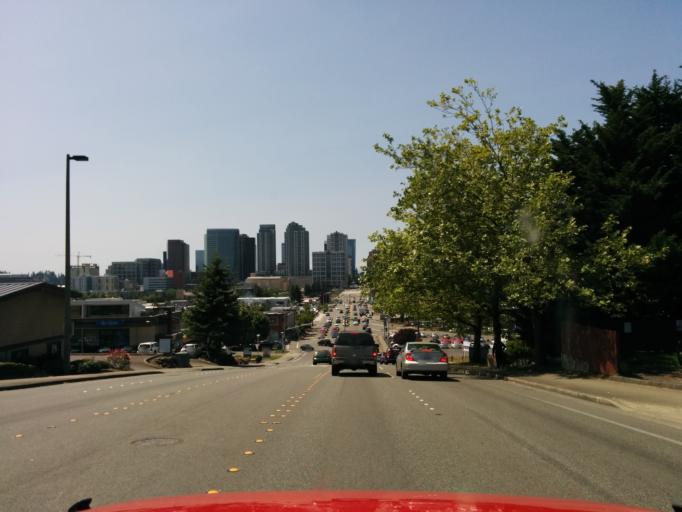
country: US
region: Washington
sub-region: King County
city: Bellevue
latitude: 47.6174
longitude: -122.1782
